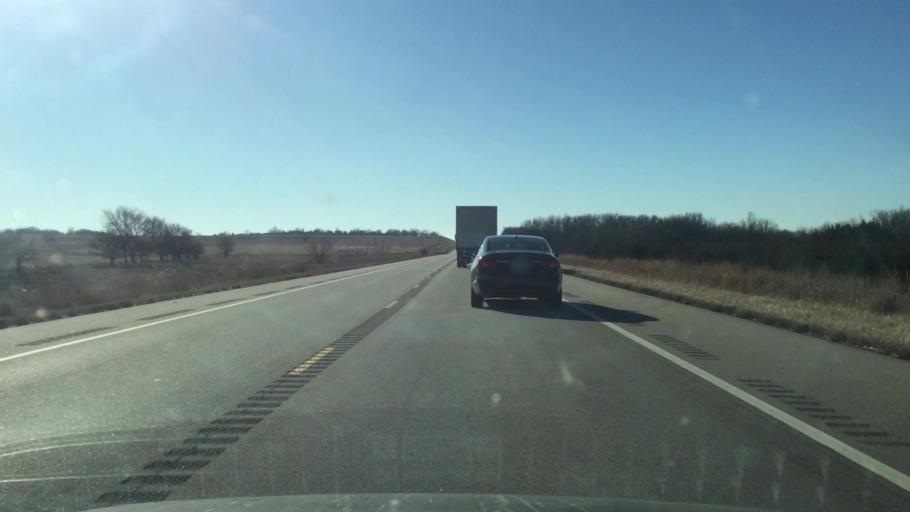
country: US
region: Kansas
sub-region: Allen County
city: Iola
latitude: 38.0229
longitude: -95.3806
